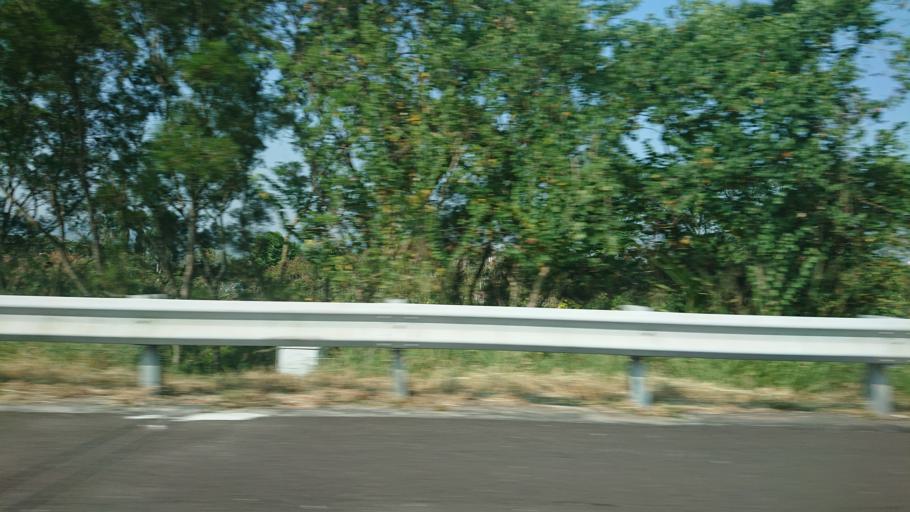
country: TW
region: Taiwan
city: Lugu
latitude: 23.8243
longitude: 120.7071
